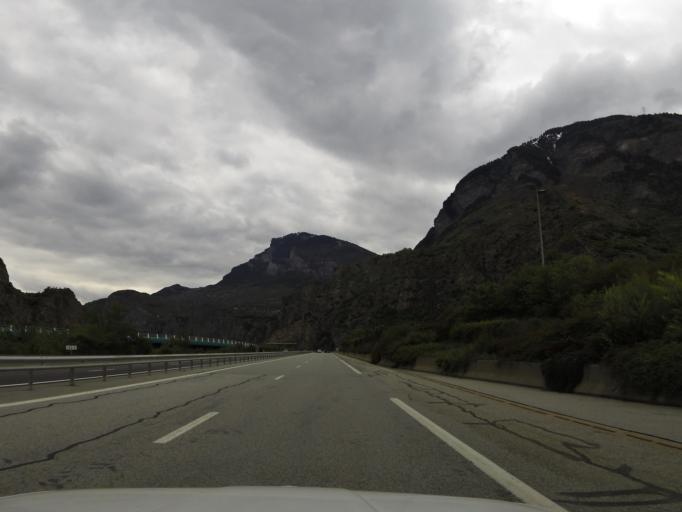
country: FR
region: Rhone-Alpes
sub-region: Departement de la Savoie
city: Saint-Jean-de-Maurienne
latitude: 45.2959
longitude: 6.3561
